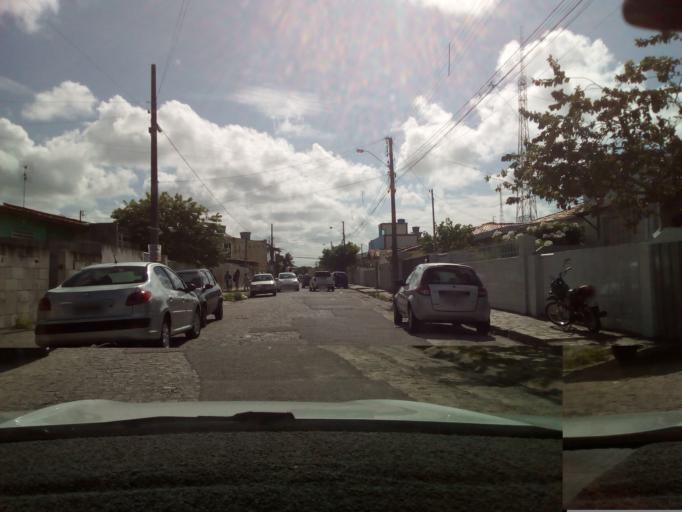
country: BR
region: Paraiba
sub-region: Joao Pessoa
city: Joao Pessoa
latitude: -7.1285
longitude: -34.8778
